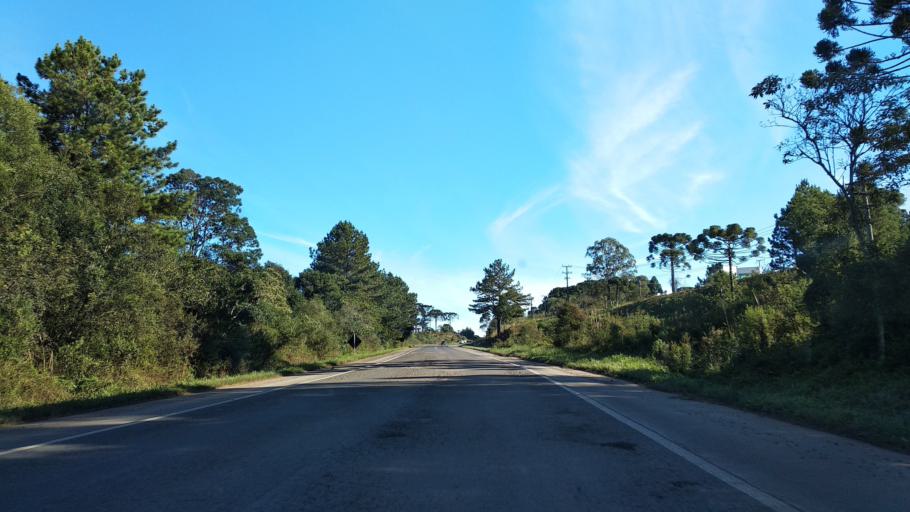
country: BR
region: Santa Catarina
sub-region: Campos Novos
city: Campos Novos
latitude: -27.4020
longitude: -51.2031
